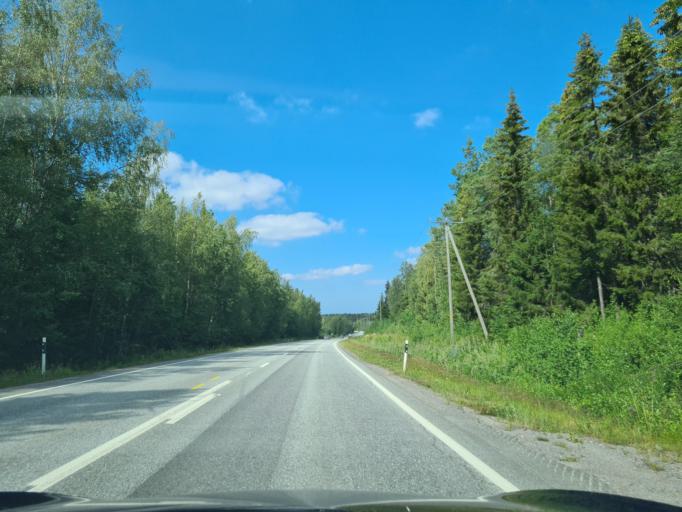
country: FI
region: Ostrobothnia
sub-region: Vaasa
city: Vaasa
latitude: 63.1847
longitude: 21.5676
